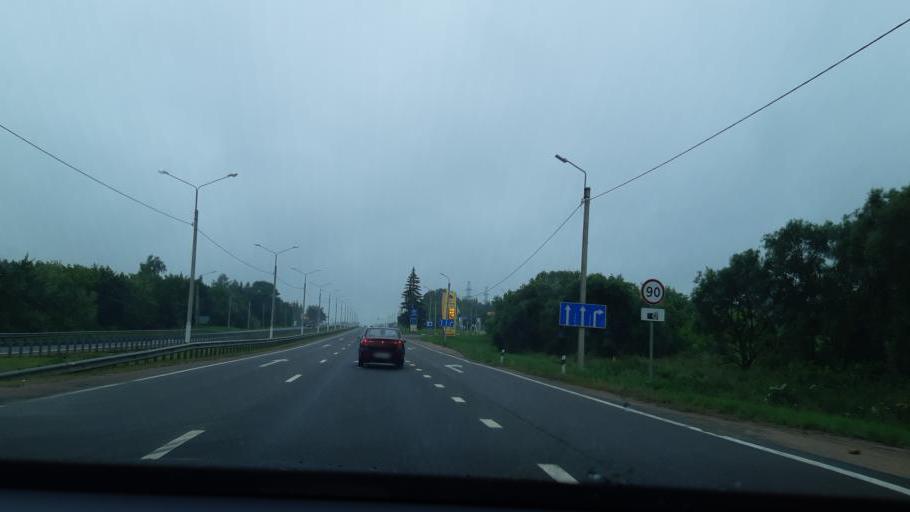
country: RU
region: Smolensk
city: Talashkino
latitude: 54.6553
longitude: 32.1639
